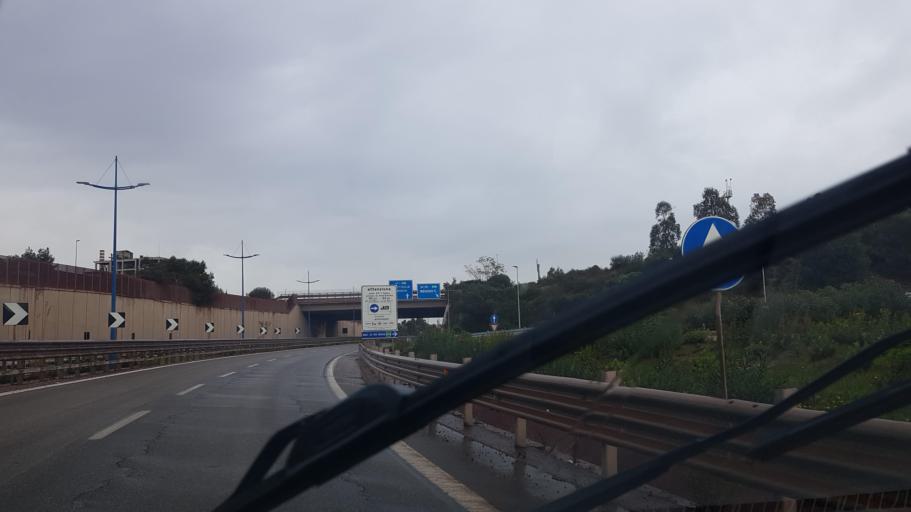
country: IT
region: Apulia
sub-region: Provincia di Taranto
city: Statte
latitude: 40.4835
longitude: 17.2056
